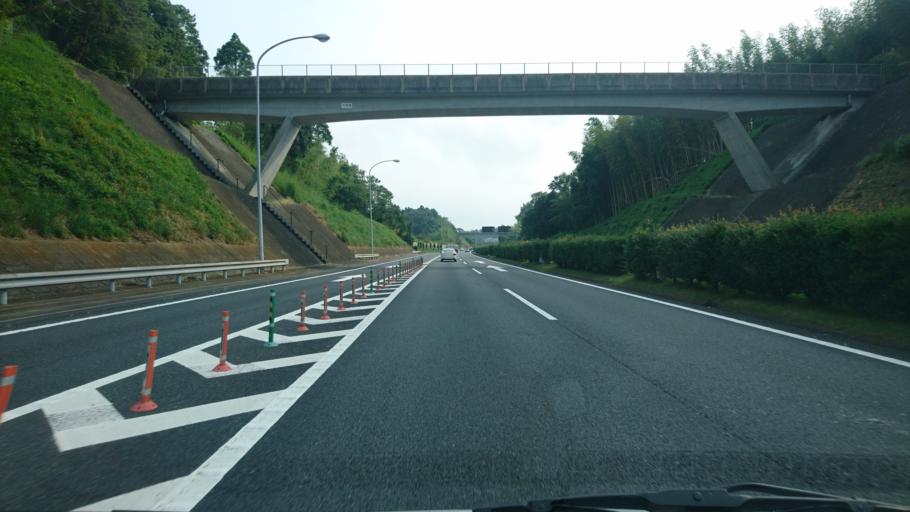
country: JP
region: Chiba
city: Narita
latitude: 35.7877
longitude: 140.3470
